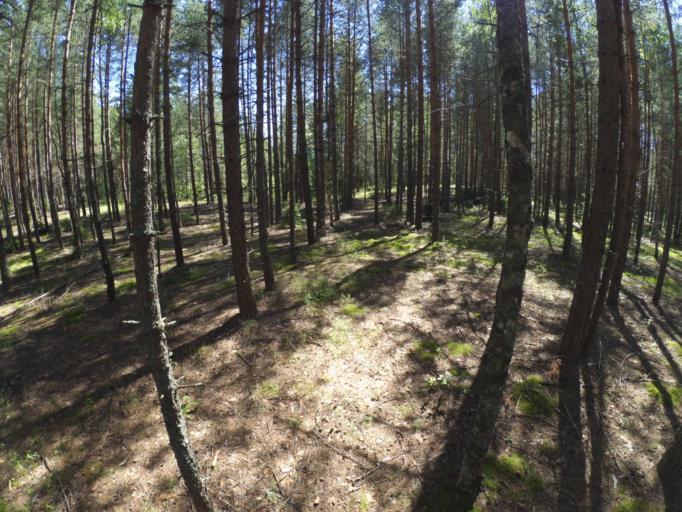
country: RU
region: Moskovskaya
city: Fosforitnyy
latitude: 55.3428
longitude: 38.9201
